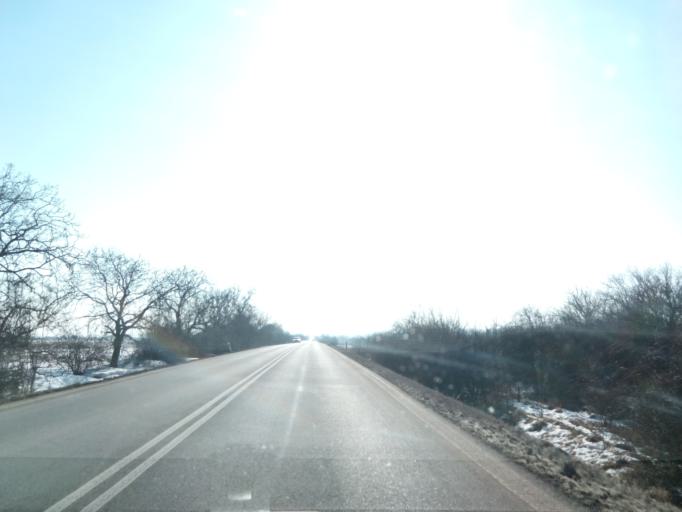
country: SK
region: Kosicky
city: Secovce
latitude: 48.7209
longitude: 21.6094
